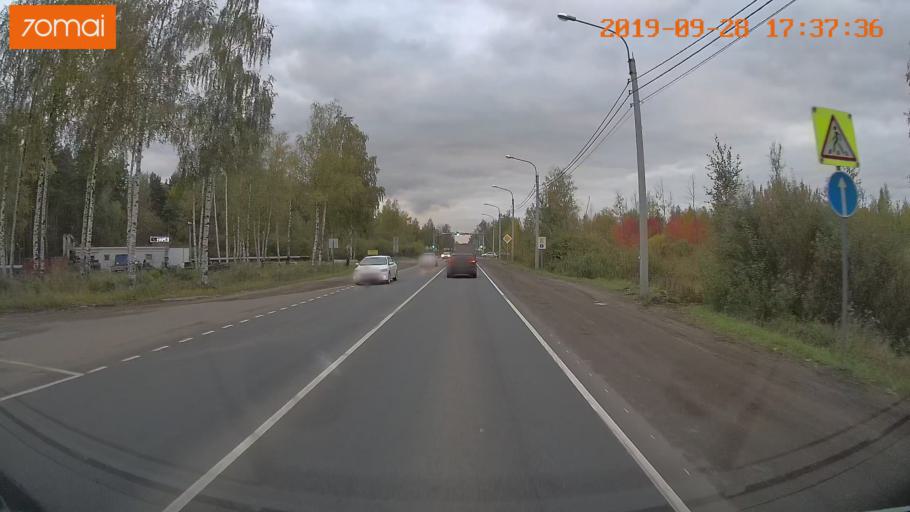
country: RU
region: Jaroslavl
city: Yaroslavl
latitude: 57.5428
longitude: 39.9480
